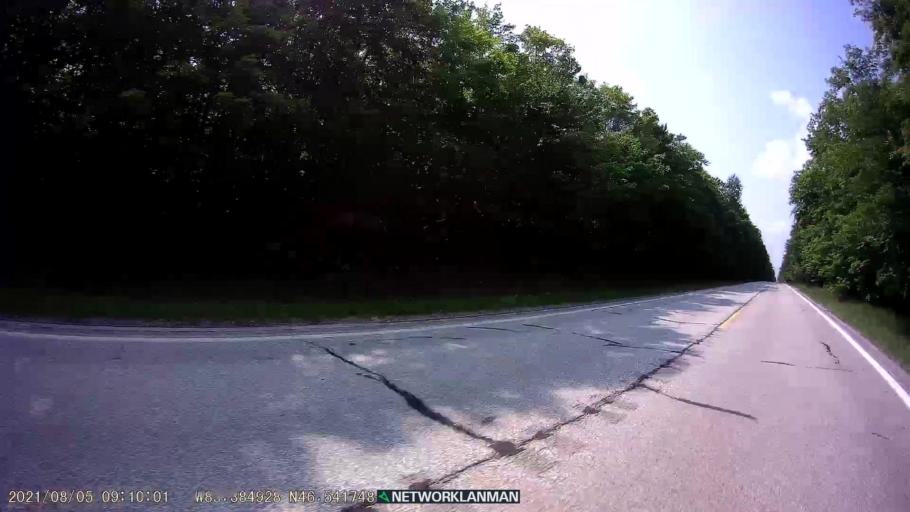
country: US
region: Michigan
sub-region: Luce County
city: Newberry
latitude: 46.5416
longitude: -85.3851
